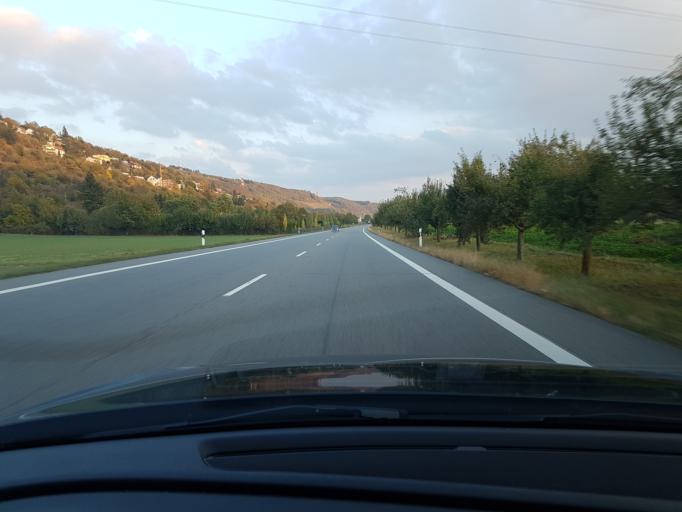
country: DE
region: Baden-Wuerttemberg
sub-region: Karlsruhe Region
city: Neckarzimmern
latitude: 49.3236
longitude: 9.1177
